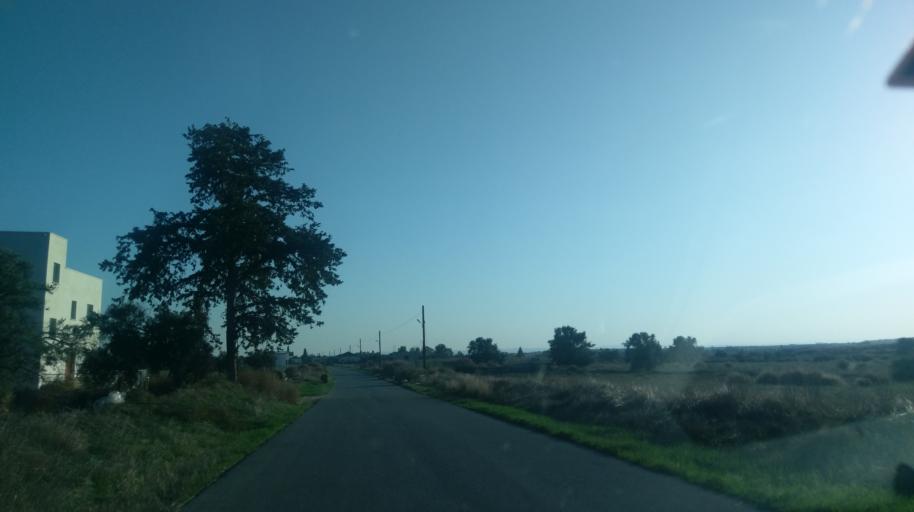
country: CY
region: Ammochostos
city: Lefkonoiko
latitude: 35.2745
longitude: 33.6579
